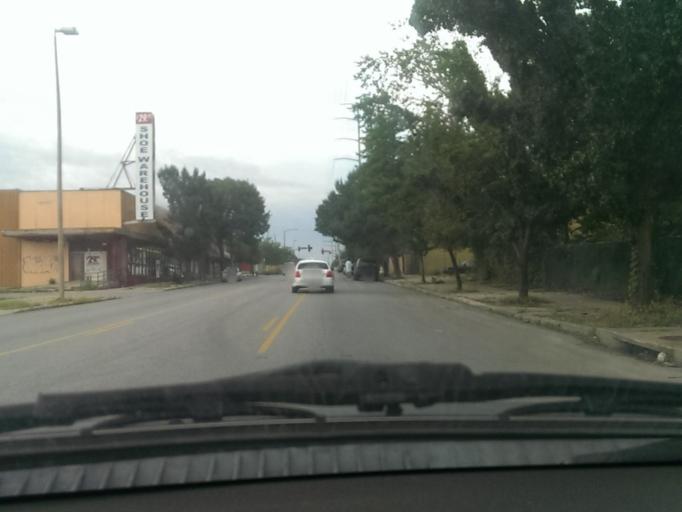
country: US
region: Missouri
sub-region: Jackson County
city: Kansas City
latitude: 39.0669
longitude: -94.5715
